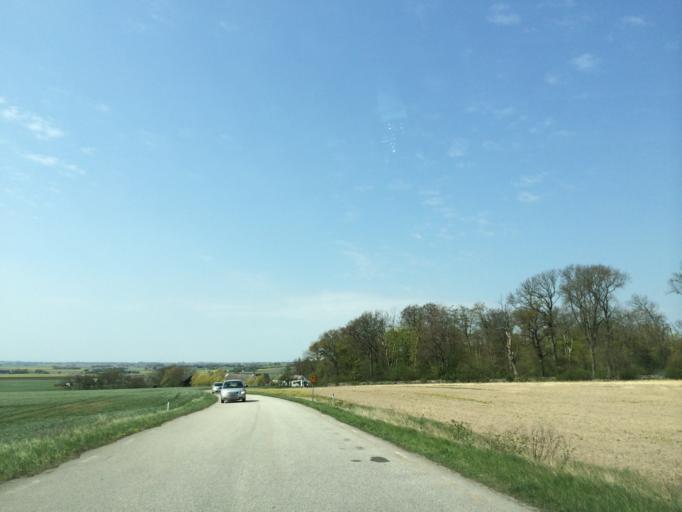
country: SE
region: Skane
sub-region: Lunds Kommun
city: Genarp
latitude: 55.6710
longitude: 13.3345
